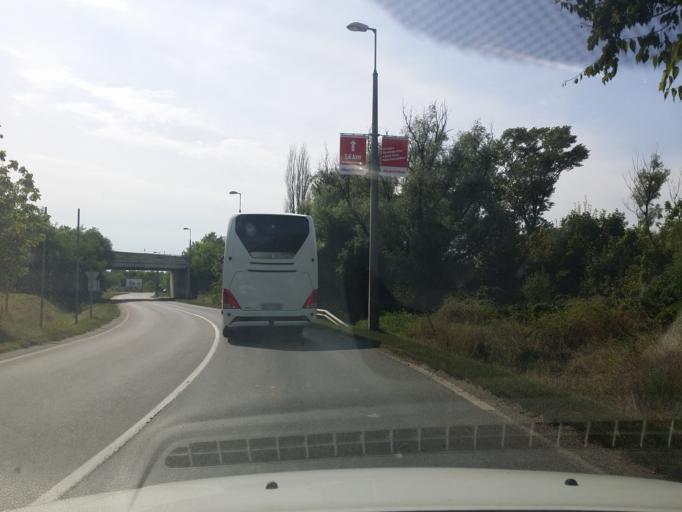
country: HU
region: Bacs-Kiskun
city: Baja
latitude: 46.1949
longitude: 18.9506
